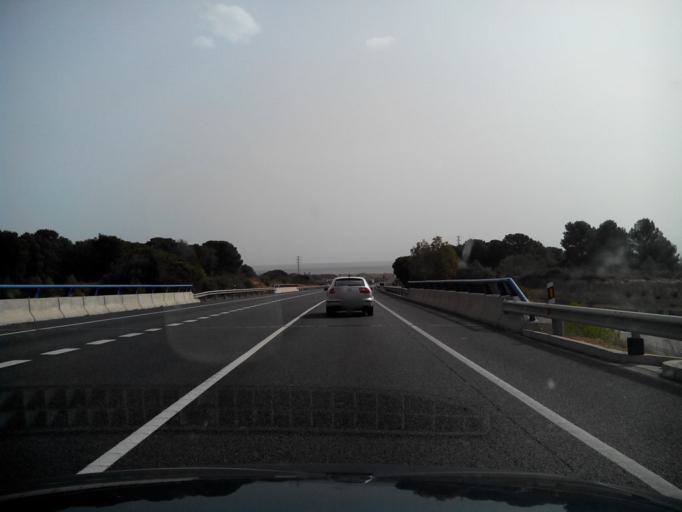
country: ES
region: Catalonia
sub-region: Provincia de Tarragona
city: Torredembarra
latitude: 41.1608
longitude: 1.4159
